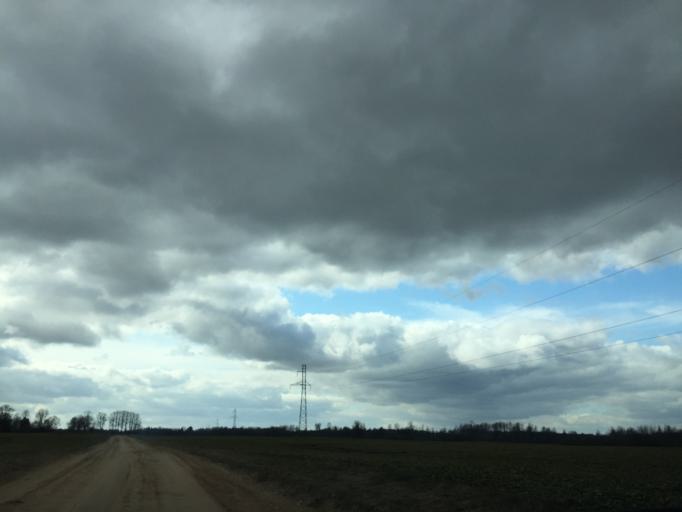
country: LV
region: Vecumnieki
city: Vecumnieki
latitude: 56.5625
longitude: 24.5977
